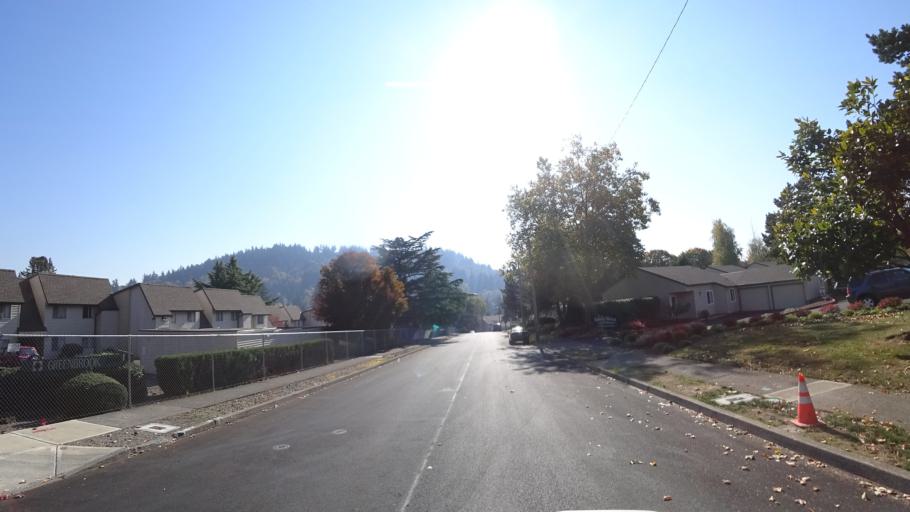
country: US
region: Oregon
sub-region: Multnomah County
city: Gresham
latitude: 45.4966
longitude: -122.4424
